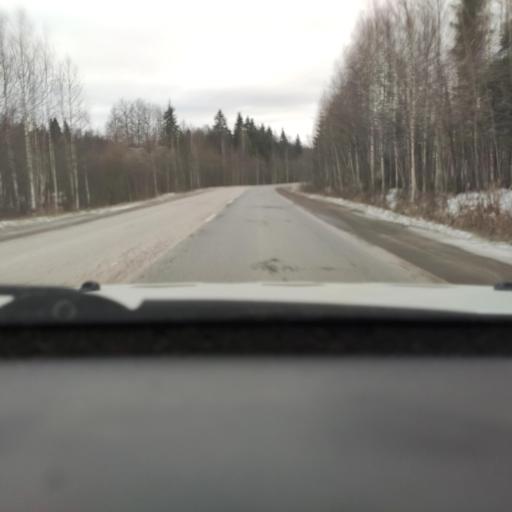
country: RU
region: Perm
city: Polazna
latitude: 58.1100
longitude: 56.4227
